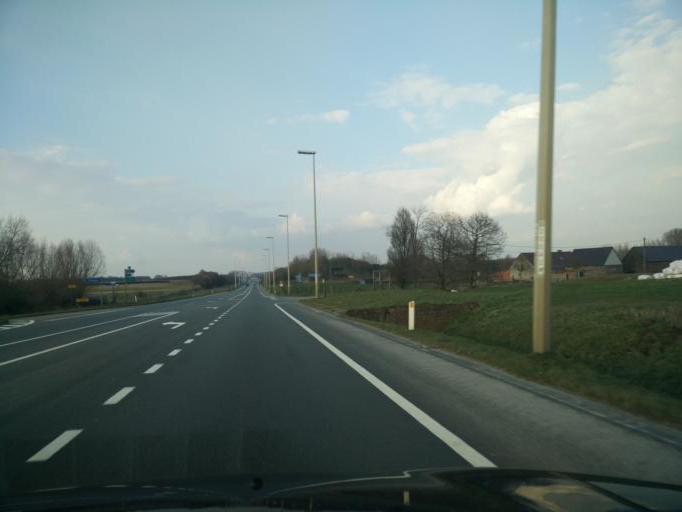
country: BE
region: Flanders
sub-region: Provincie Oost-Vlaanderen
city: Oosterzele
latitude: 50.9280
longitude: 3.8180
